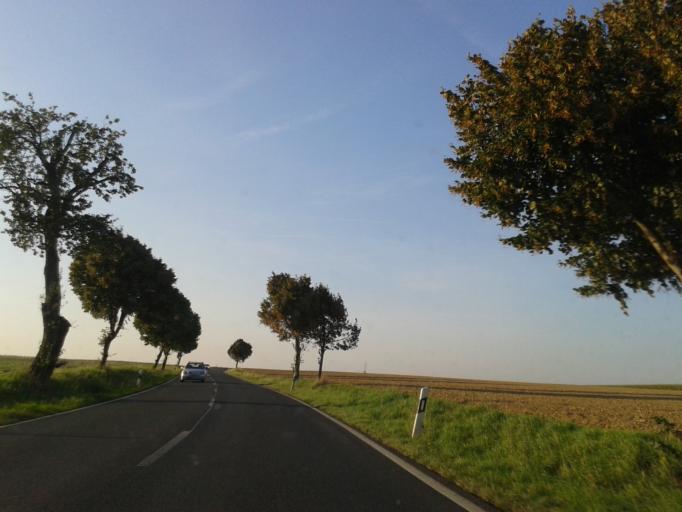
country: DE
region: Saxony
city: Klipphausen
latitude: 51.0816
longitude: 13.5017
